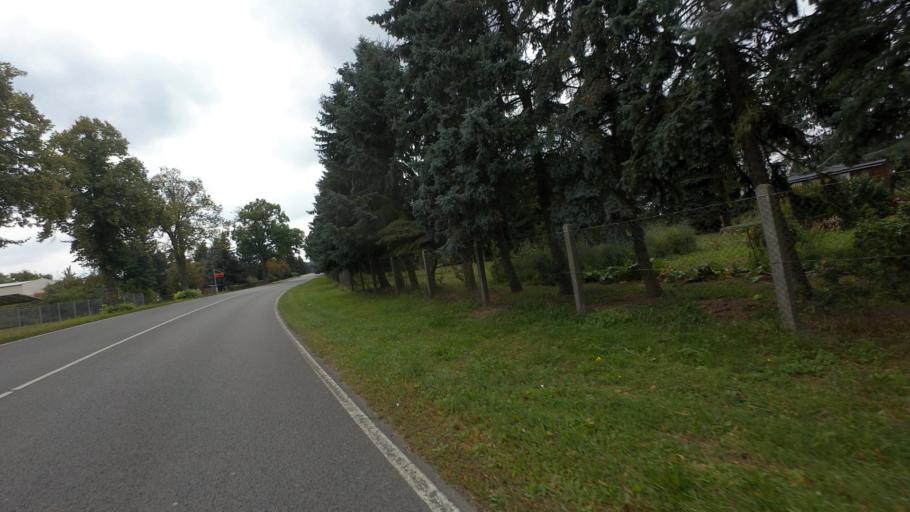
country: DE
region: Brandenburg
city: Sonnewalde
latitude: 51.6798
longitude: 13.6454
